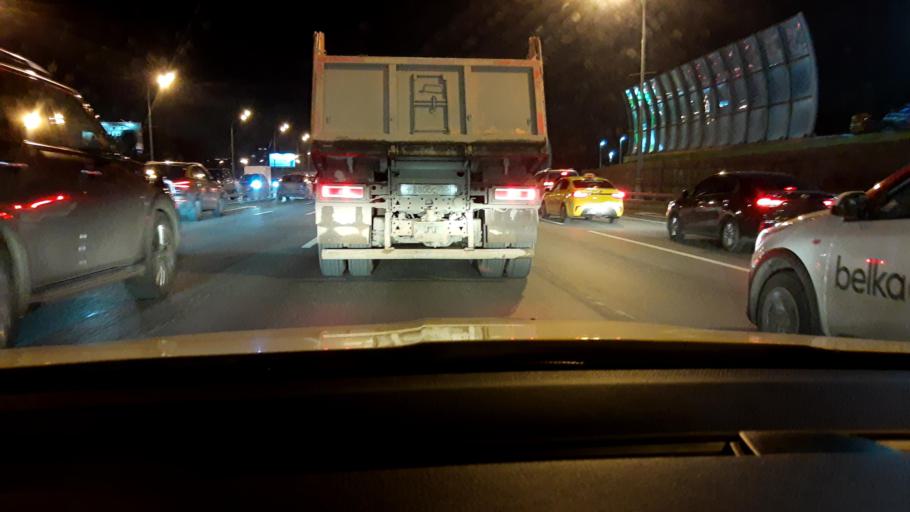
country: RU
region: Moscow
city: Novyye Cheremushki
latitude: 55.7038
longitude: 37.6030
